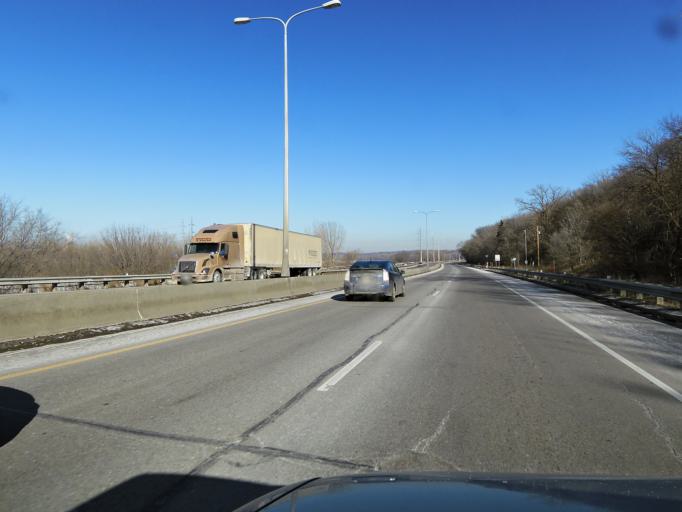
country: US
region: Minnesota
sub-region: Dakota County
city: South Saint Paul
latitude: 44.9076
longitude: -93.0125
